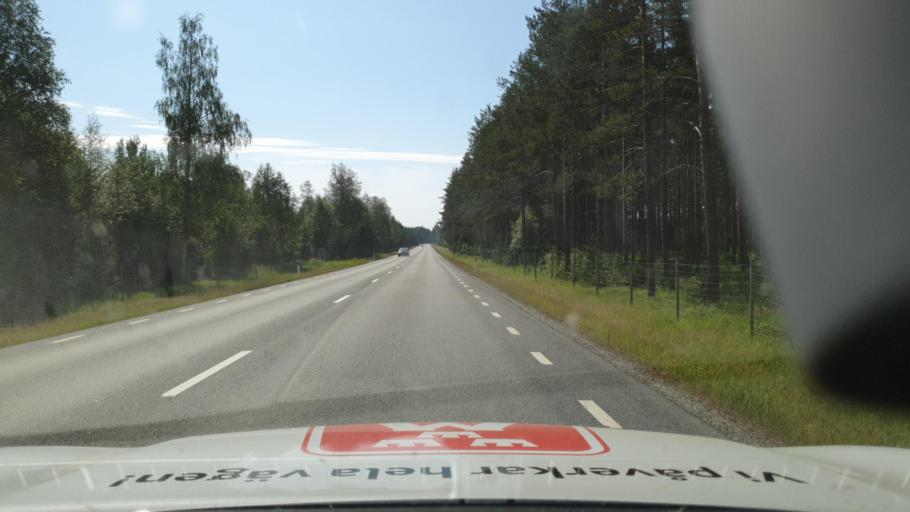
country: SE
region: Vaesterbotten
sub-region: Skelleftea Kommun
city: Burea
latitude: 64.5593
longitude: 21.2370
